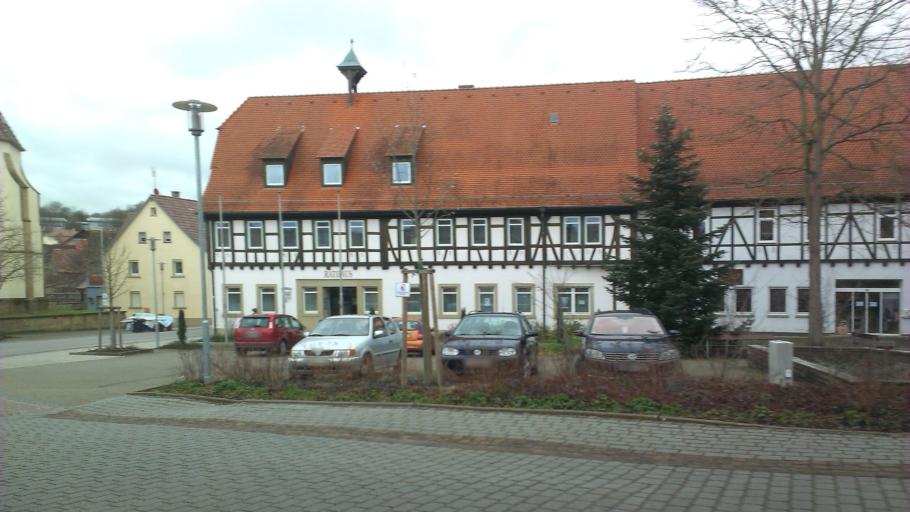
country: DE
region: Baden-Wuerttemberg
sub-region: Karlsruhe Region
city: Kurnbach
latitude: 49.0778
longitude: 8.8451
